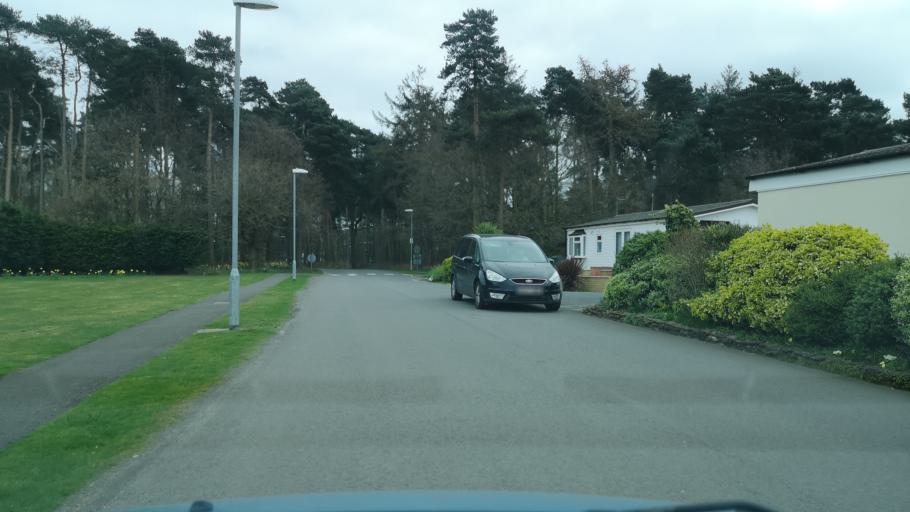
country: GB
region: England
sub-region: North Lincolnshire
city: Scunthorpe
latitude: 53.5697
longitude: -0.6861
